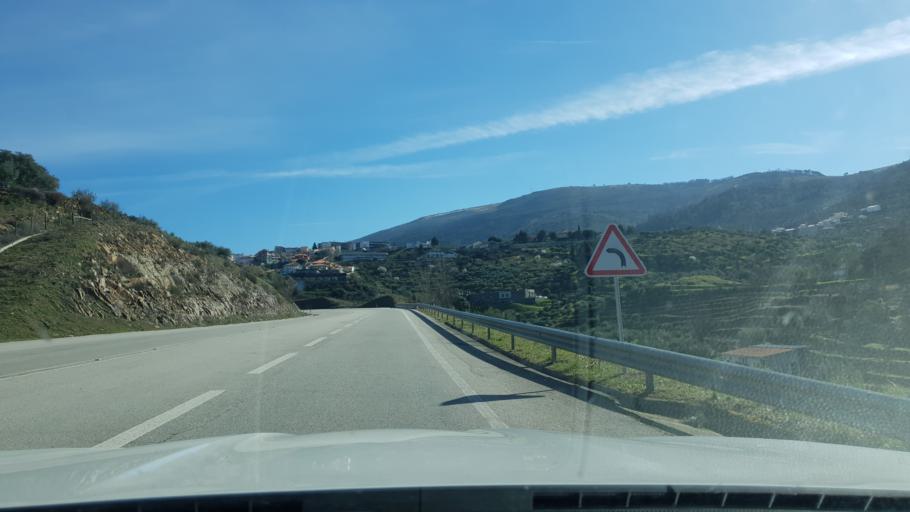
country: PT
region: Braganca
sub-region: Torre de Moncorvo
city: Torre de Moncorvo
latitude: 41.1773
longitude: -7.0672
